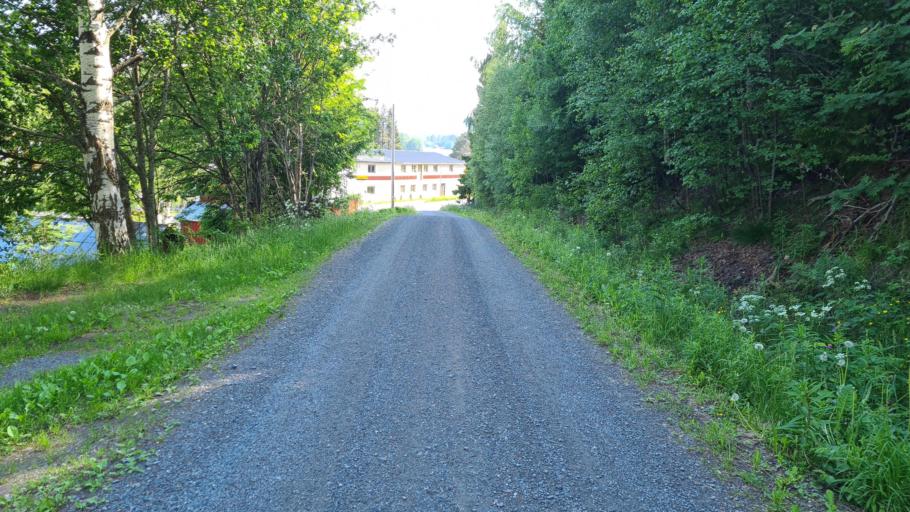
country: SE
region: Vaesternorrland
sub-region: Kramfors Kommun
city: Nordingra
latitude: 62.9831
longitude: 18.4188
